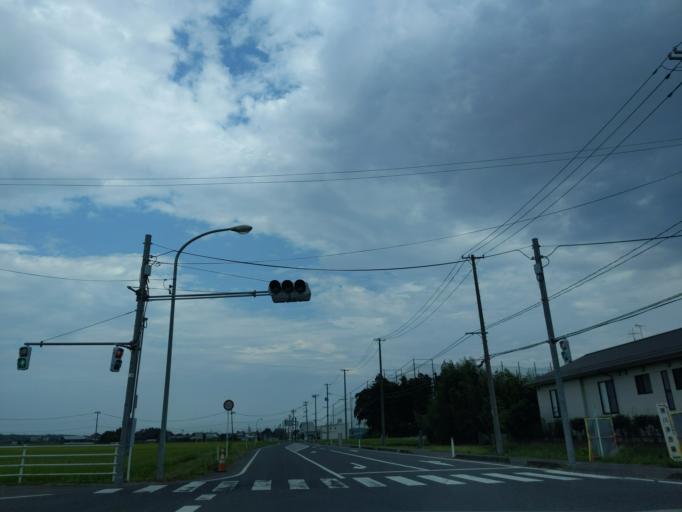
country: JP
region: Miyagi
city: Tomiya
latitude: 38.4334
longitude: 140.8826
